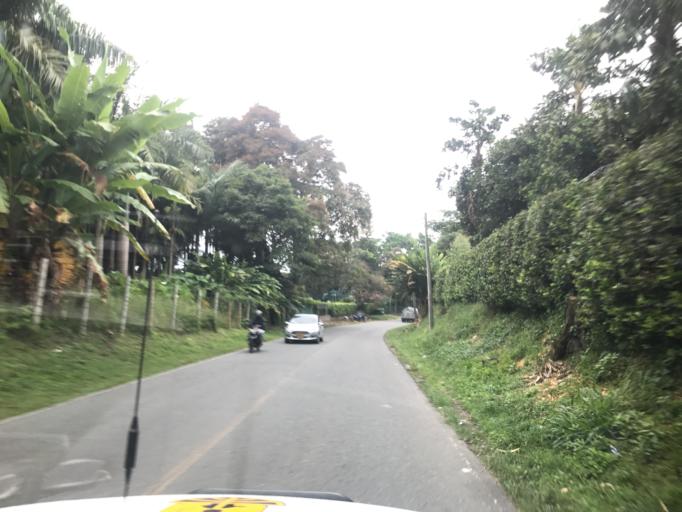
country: CO
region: Quindio
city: Montenegro
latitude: 4.5595
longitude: -75.7620
